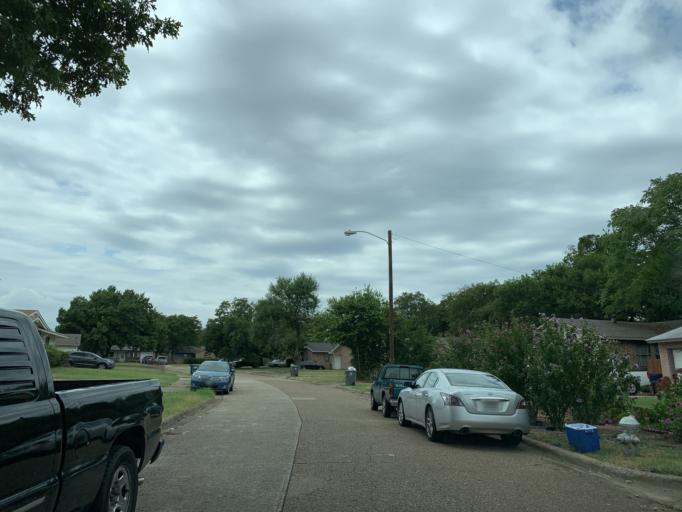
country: US
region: Texas
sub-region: Dallas County
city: DeSoto
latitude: 32.6564
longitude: -96.8297
